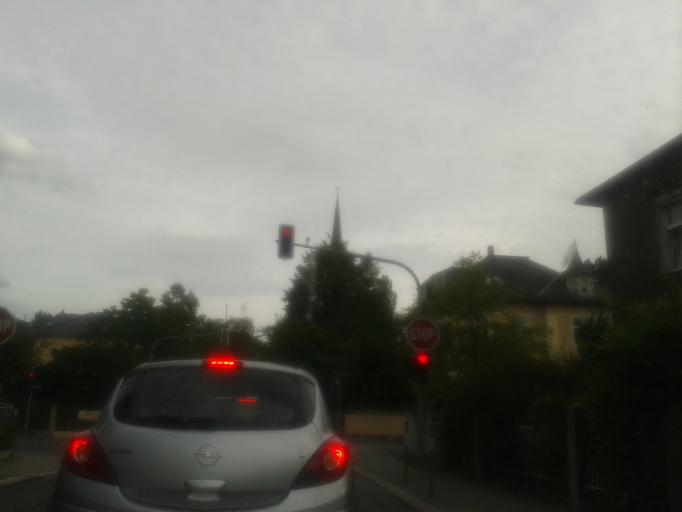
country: DE
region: Saxony
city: Albertstadt
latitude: 51.0497
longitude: 13.8056
